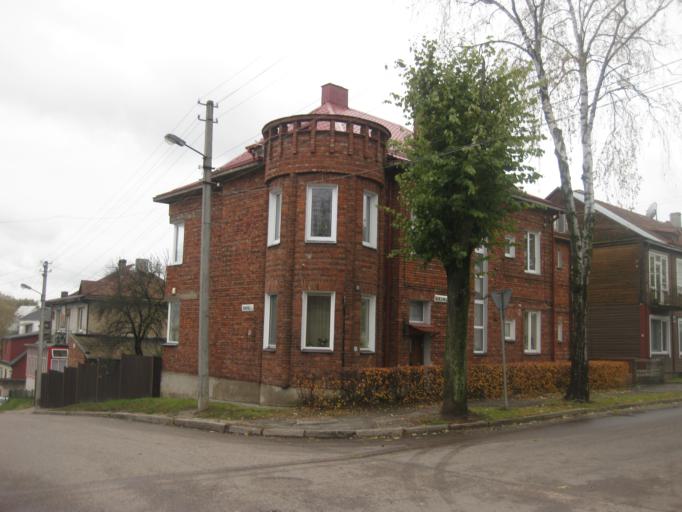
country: LT
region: Kauno apskritis
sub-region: Kaunas
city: Kaunas
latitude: 54.9069
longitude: 23.9151
